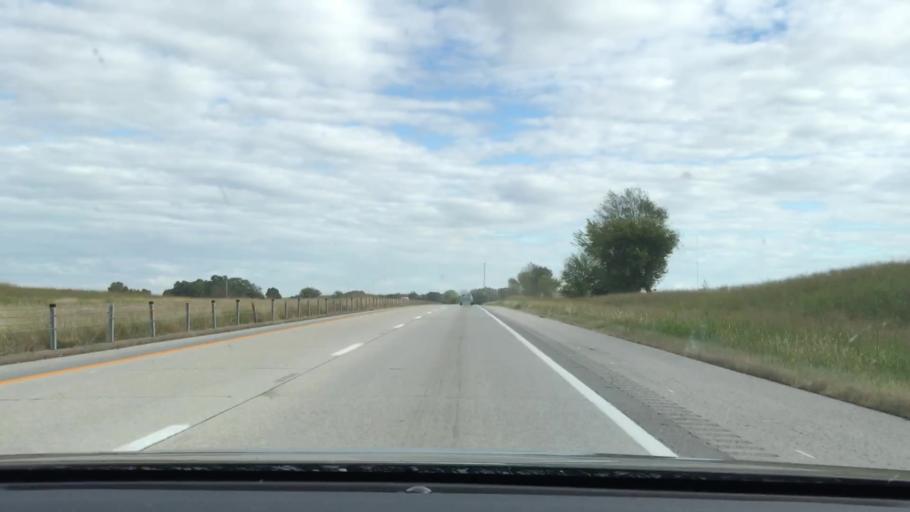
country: US
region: Kentucky
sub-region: Christian County
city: Hopkinsville
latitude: 36.8217
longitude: -87.6485
